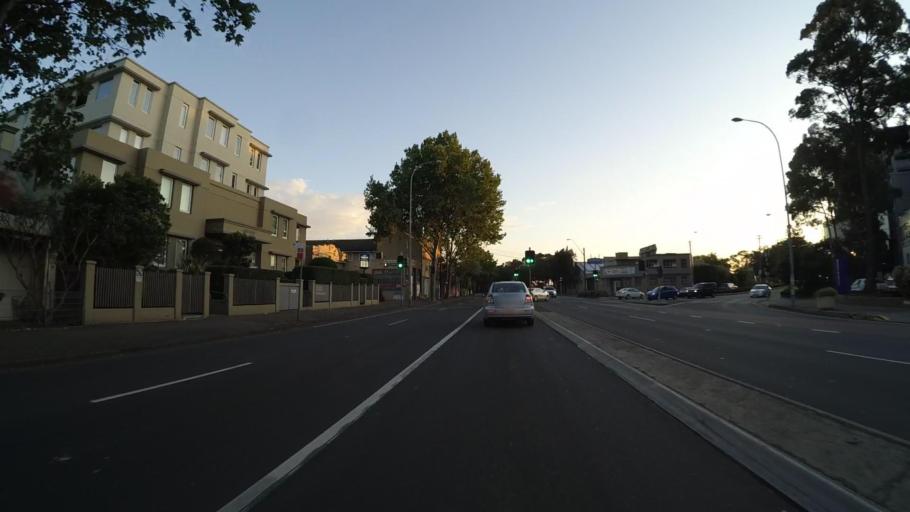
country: AU
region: New South Wales
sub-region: Botany Bay
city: Mascot
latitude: -33.9329
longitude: 151.1936
